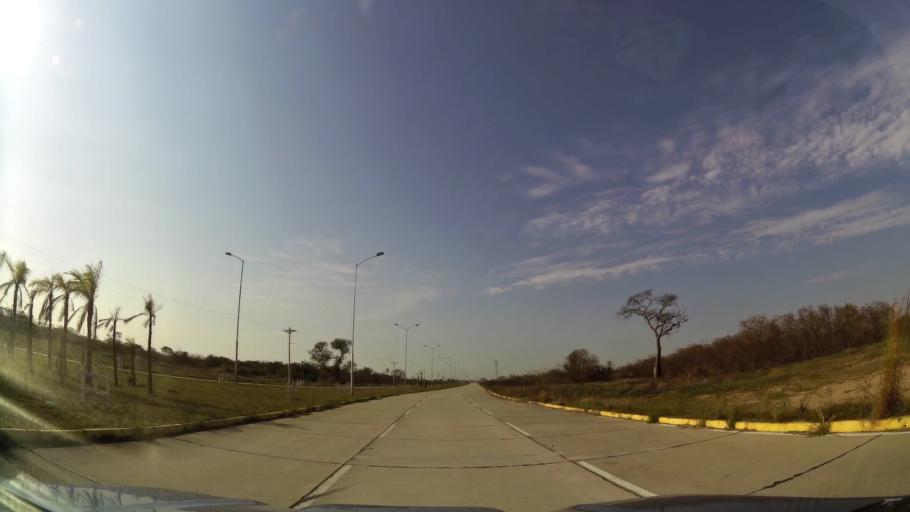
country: BO
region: Santa Cruz
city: Santa Cruz de la Sierra
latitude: -17.6695
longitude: -63.1289
